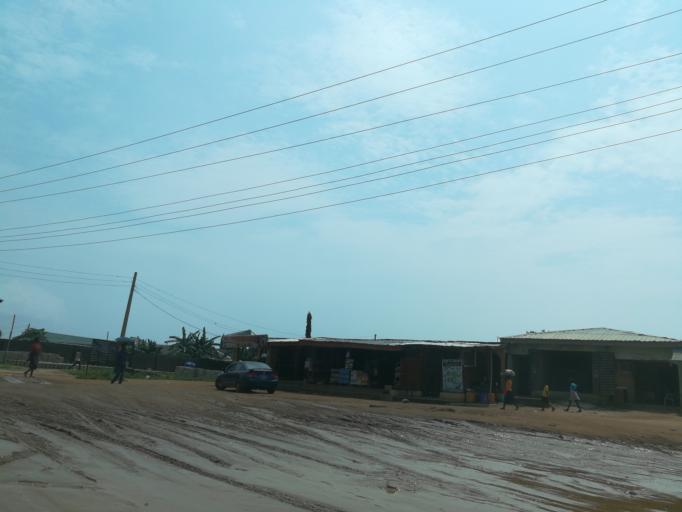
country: NG
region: Lagos
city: Ikorodu
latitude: 6.5880
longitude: 3.6245
